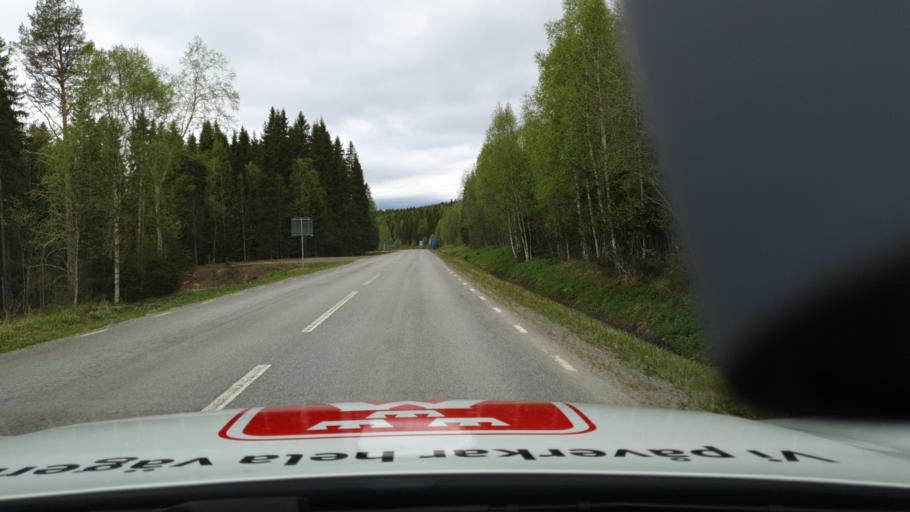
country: NO
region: Nord-Trondelag
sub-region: Lierne
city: Sandvika
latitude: 64.4776
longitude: 14.0913
